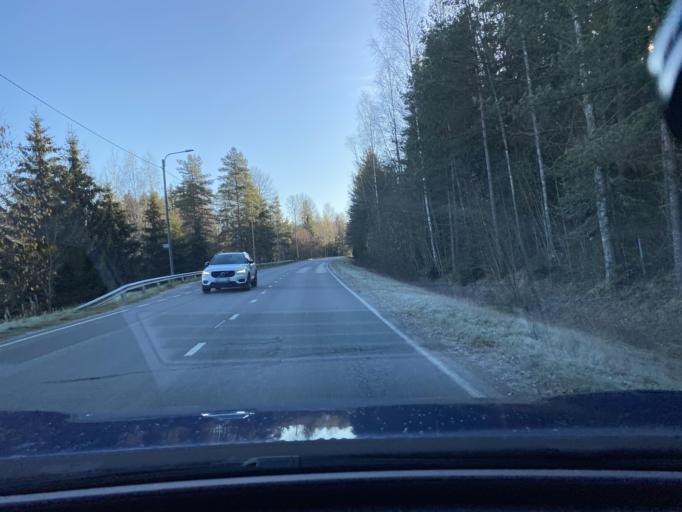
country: FI
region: Pirkanmaa
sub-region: Etelae-Pirkanmaa
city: Kylmaekoski
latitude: 61.0660
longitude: 23.6355
